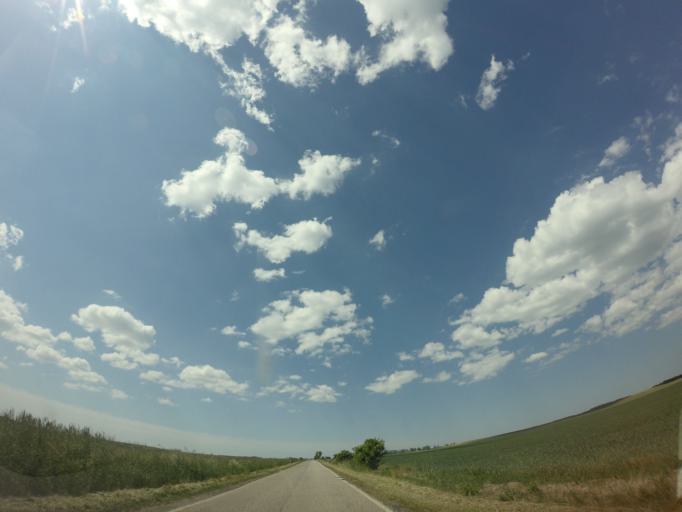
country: PL
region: West Pomeranian Voivodeship
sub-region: Powiat stargardzki
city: Dolice
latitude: 53.1654
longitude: 15.2274
